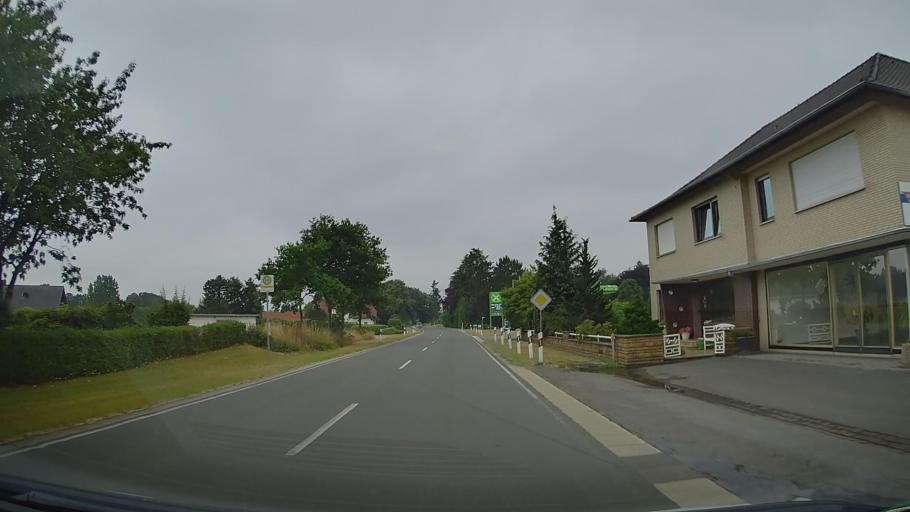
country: DE
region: North Rhine-Westphalia
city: Rahden
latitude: 52.4639
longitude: 8.5420
